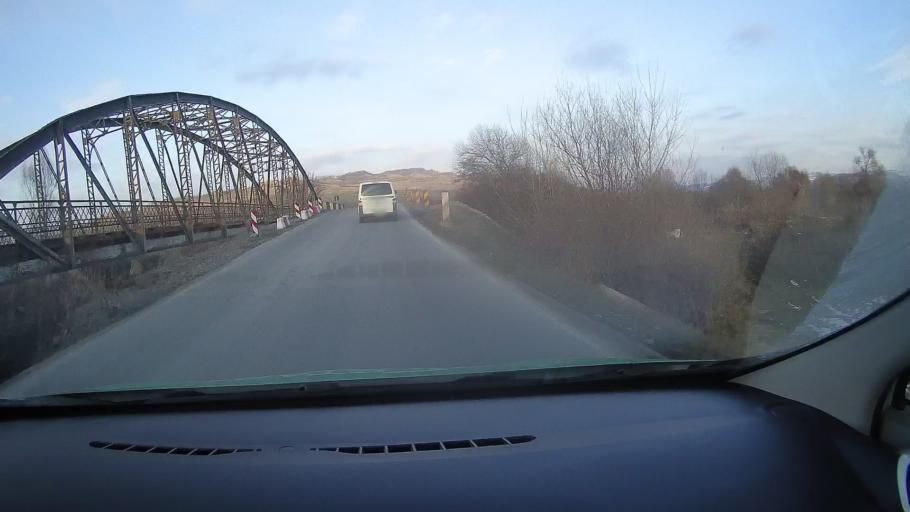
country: RO
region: Mures
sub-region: Comuna Vanatori
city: Vanatori
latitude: 46.2492
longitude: 24.9307
